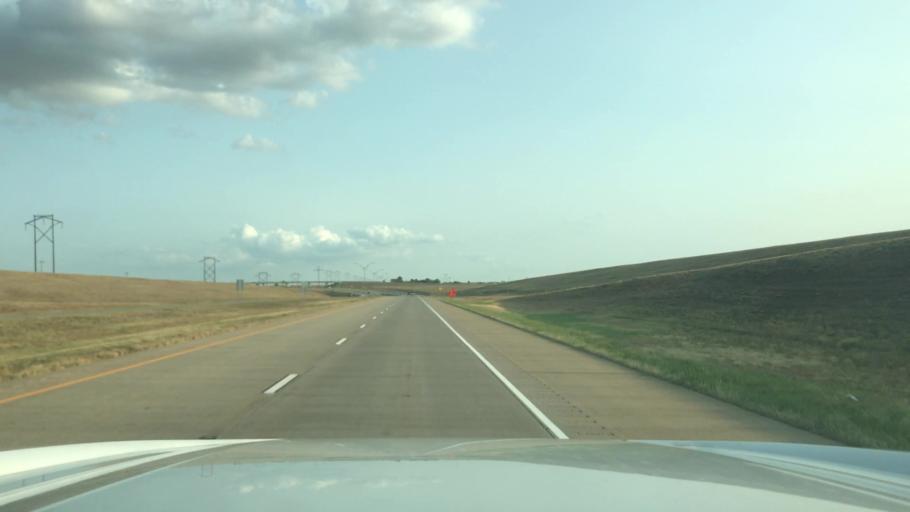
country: US
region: Texas
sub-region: Swisher County
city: Tulia
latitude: 34.5259
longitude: -101.7956
